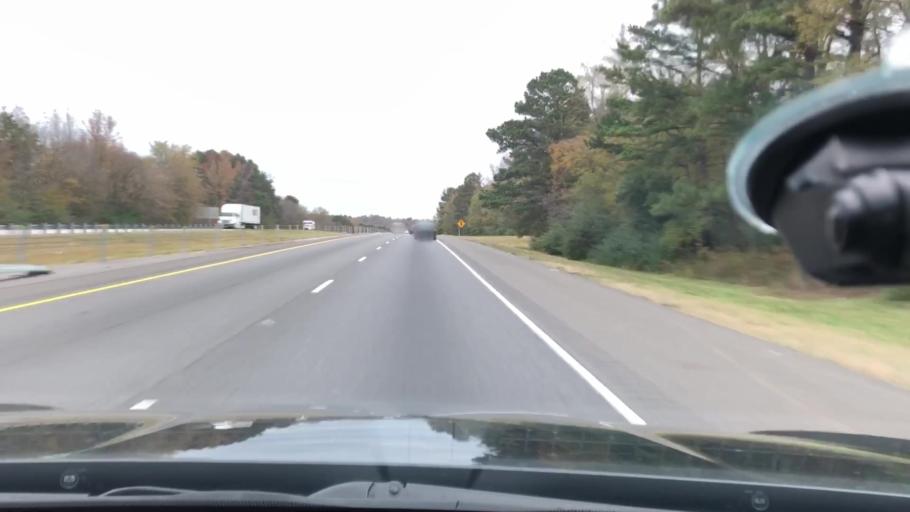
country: US
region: Arkansas
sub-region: Hot Spring County
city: Malvern
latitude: 34.3336
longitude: -92.9184
